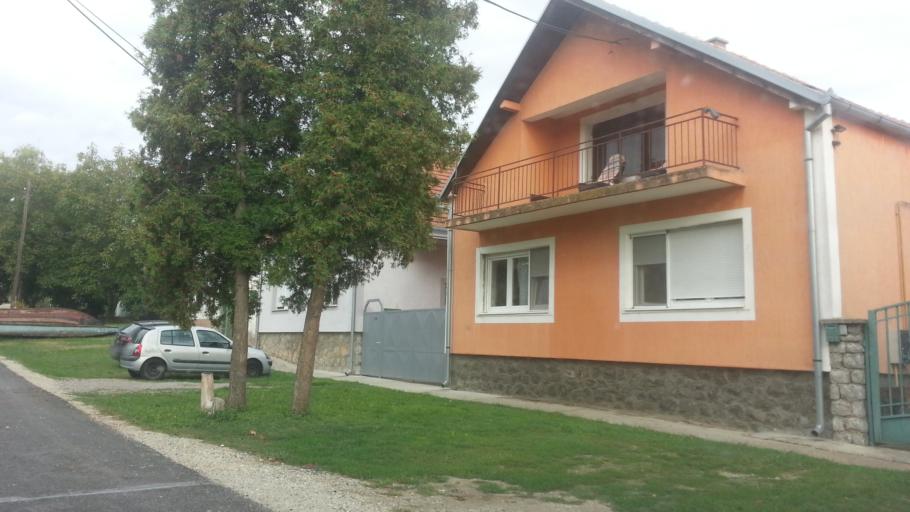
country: RS
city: Novi Banovci
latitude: 44.9563
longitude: 20.2855
